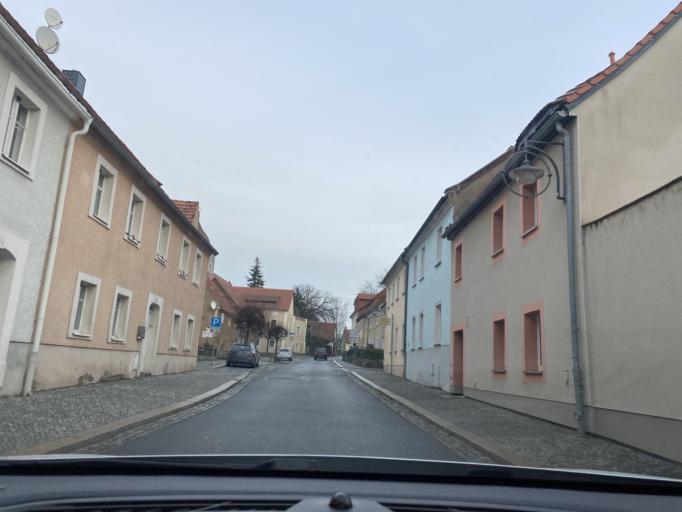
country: DE
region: Saxony
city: Reichenbach
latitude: 51.1405
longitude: 14.8016
